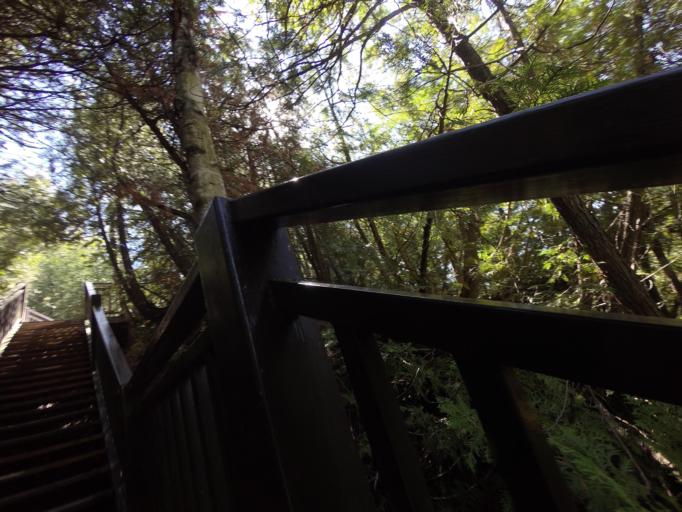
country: CA
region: Ontario
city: Orangeville
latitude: 43.8214
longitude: -80.0216
